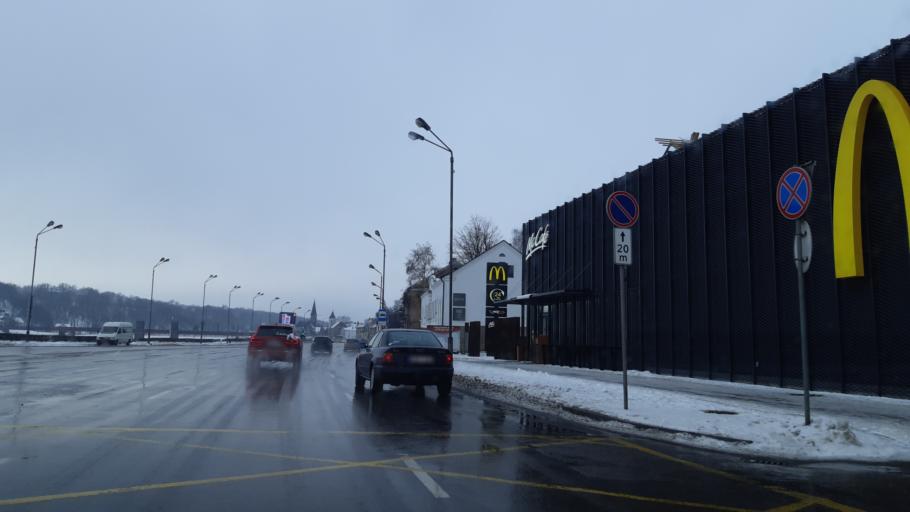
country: LT
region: Kauno apskritis
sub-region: Kaunas
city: Kaunas
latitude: 54.8943
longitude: 23.8987
